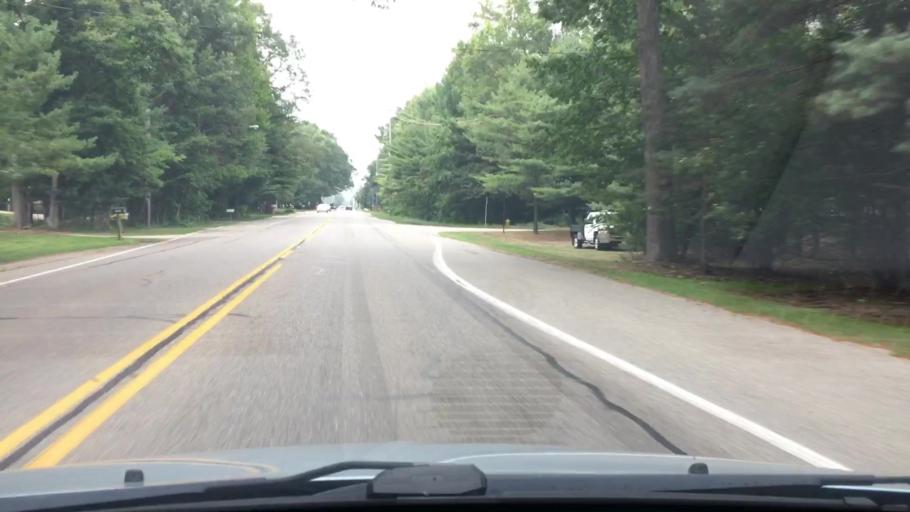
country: US
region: Michigan
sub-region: Ottawa County
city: Hudsonville
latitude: 42.9004
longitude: -85.9019
